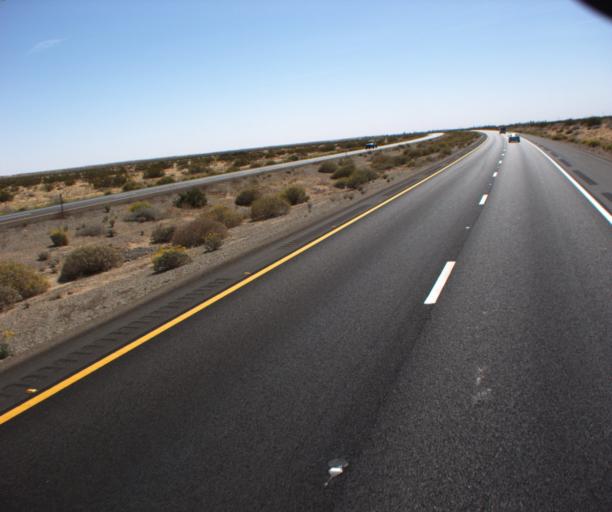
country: US
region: Arizona
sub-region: Yuma County
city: Fortuna Foothills
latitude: 32.5989
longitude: -114.5424
